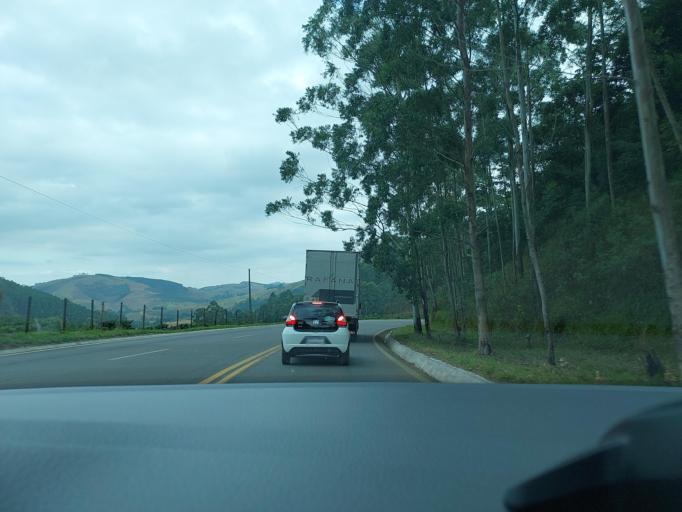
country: BR
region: Minas Gerais
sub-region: Mirai
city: Mirai
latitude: -20.9652
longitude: -42.5913
